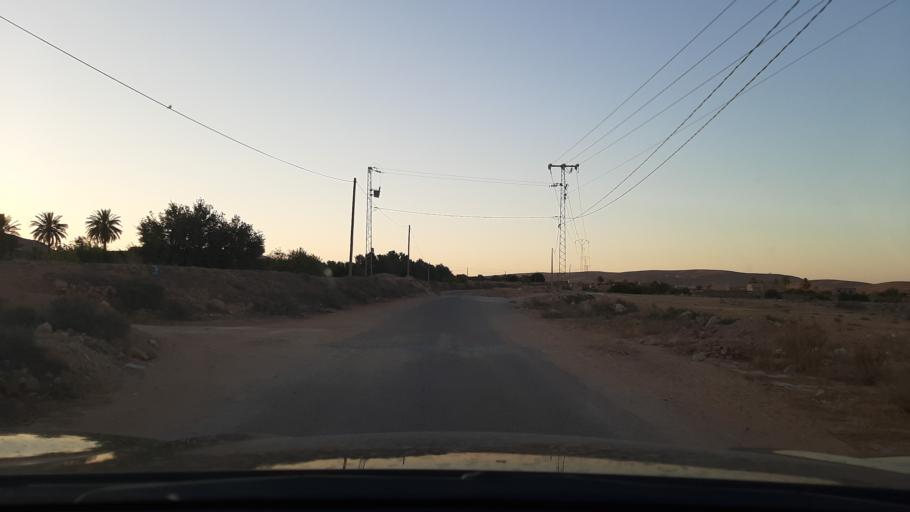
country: TN
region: Qabis
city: Matmata
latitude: 33.5534
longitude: 10.1864
